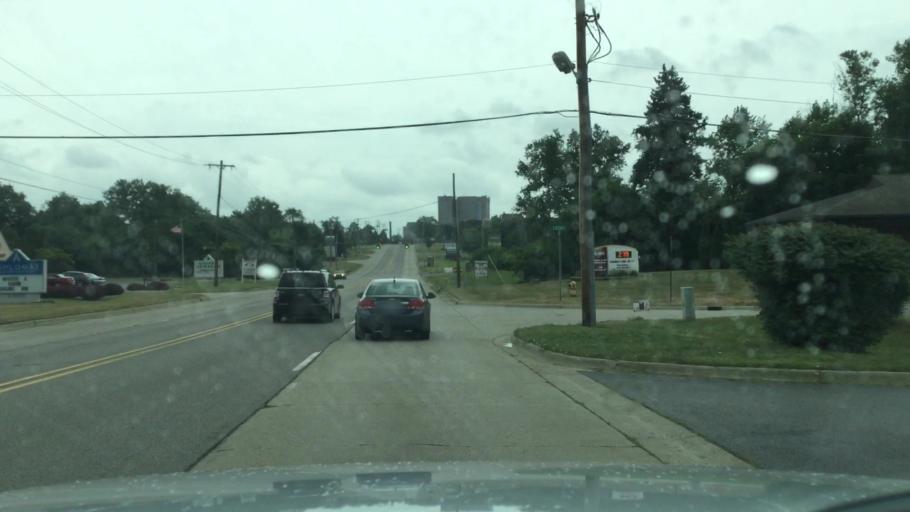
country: US
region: Michigan
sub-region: Genesee County
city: Flint
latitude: 43.0160
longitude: -83.7437
